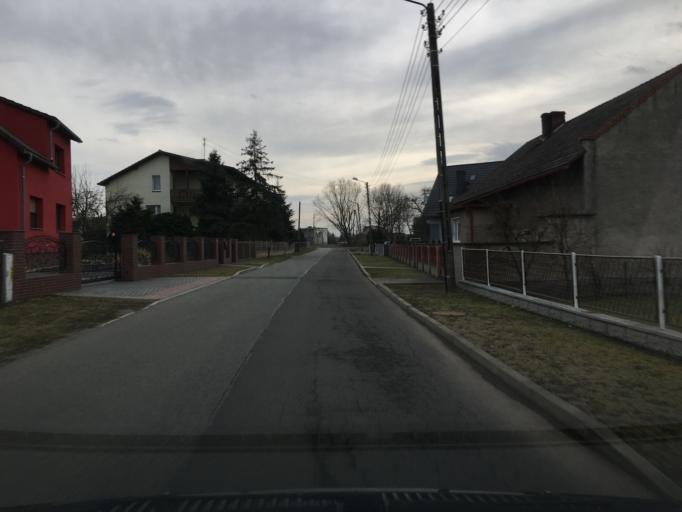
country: PL
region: Opole Voivodeship
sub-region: Powiat kedzierzynsko-kozielski
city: Wiekszyce
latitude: 50.3542
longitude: 18.1187
